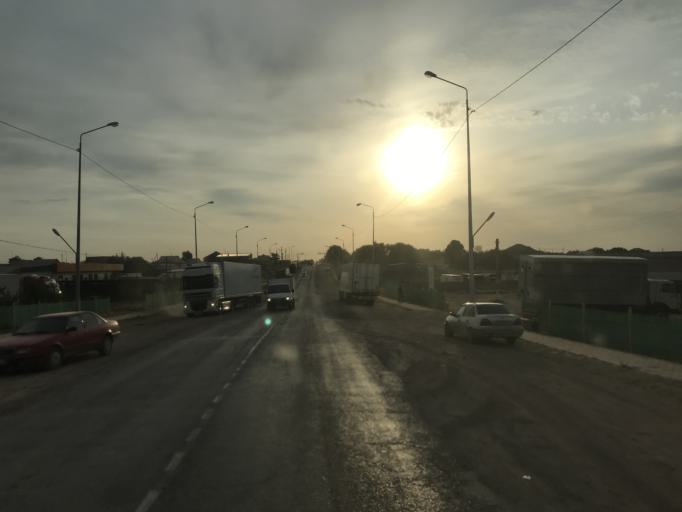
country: KZ
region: Ongtustik Qazaqstan
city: Saryaghash
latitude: 41.4295
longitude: 69.1037
